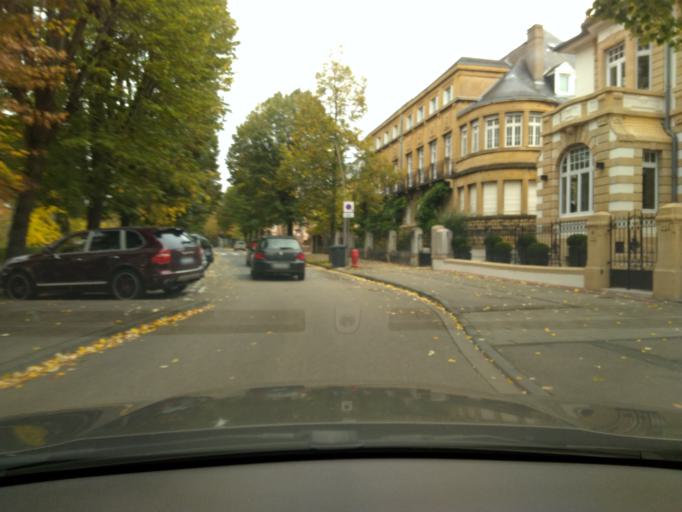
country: FR
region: Lorraine
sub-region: Departement de la Moselle
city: Metz
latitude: 49.1102
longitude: 6.1641
